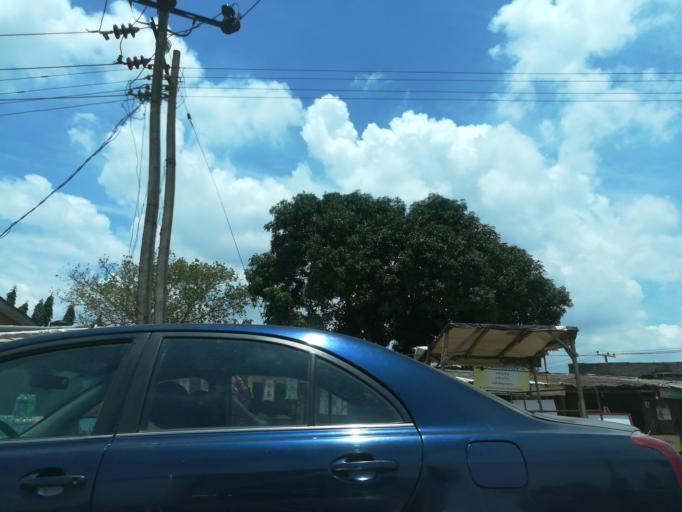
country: NG
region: Lagos
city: Ebute Ikorodu
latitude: 6.6018
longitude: 3.4918
